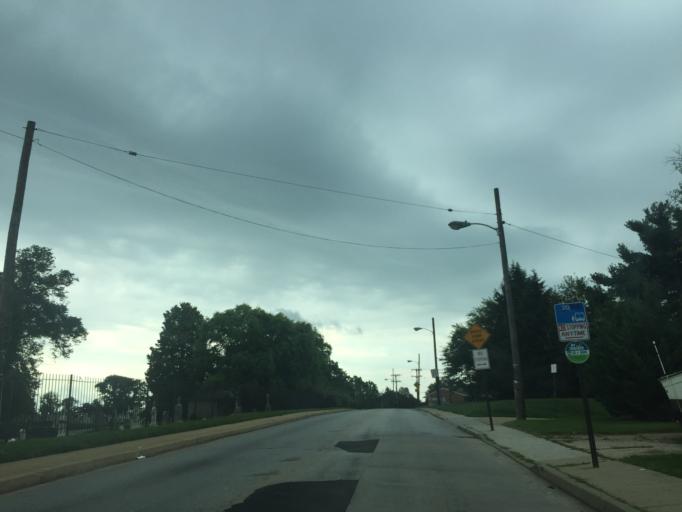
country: US
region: Maryland
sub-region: Baltimore County
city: Charlestown
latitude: 39.2881
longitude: -76.6886
